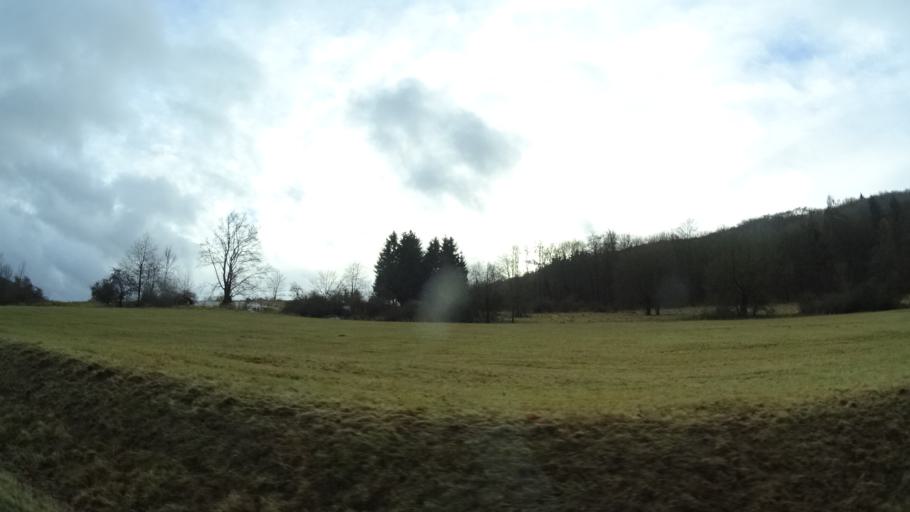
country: DE
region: Thuringia
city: Aschenhausen
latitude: 50.6043
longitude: 10.1976
